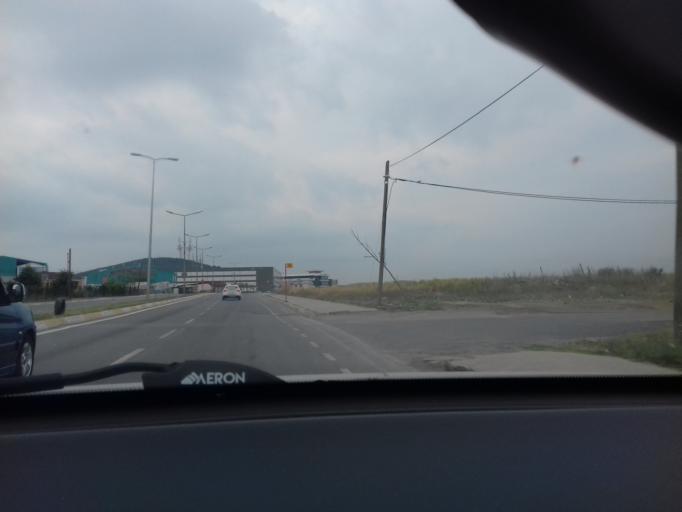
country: TR
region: Istanbul
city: Icmeler
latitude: 40.8885
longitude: 29.3529
